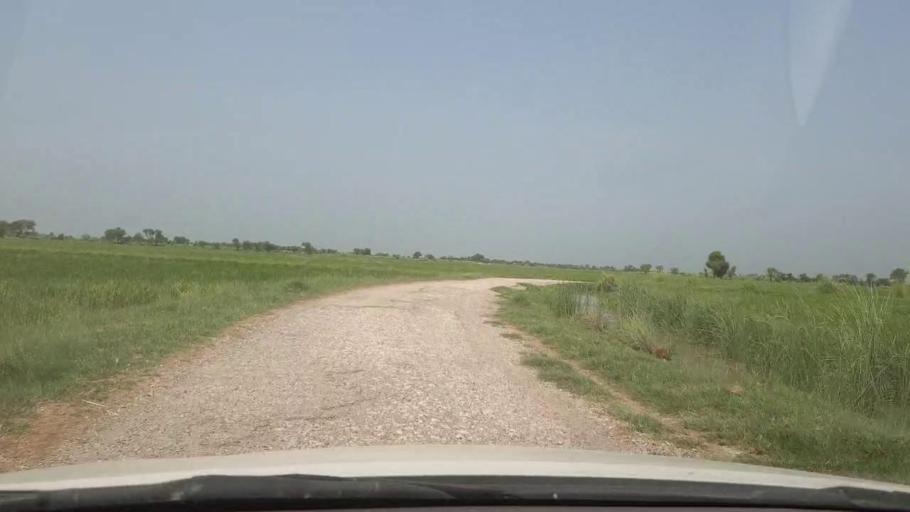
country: PK
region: Sindh
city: Shikarpur
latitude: 28.0739
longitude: 68.5740
